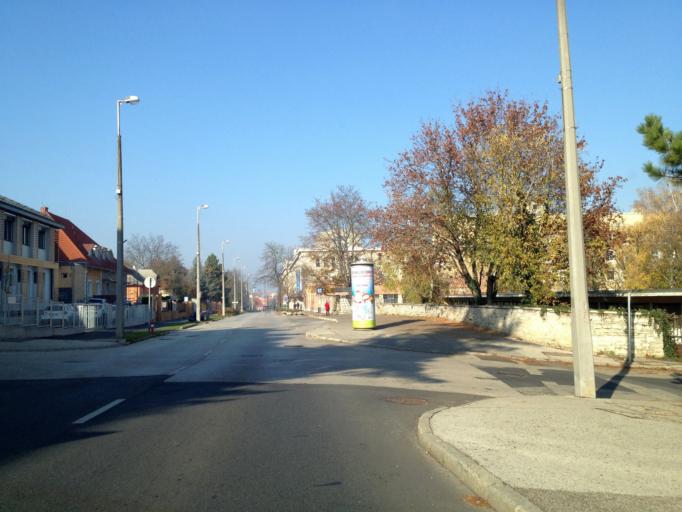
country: HU
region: Veszprem
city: Veszprem
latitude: 47.0858
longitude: 17.9089
